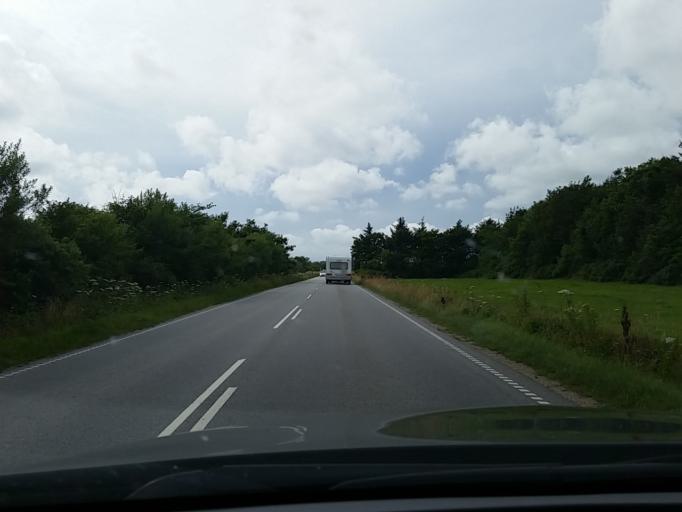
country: DK
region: South Denmark
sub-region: Varde Kommune
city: Oksbol
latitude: 55.7821
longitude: 8.2737
